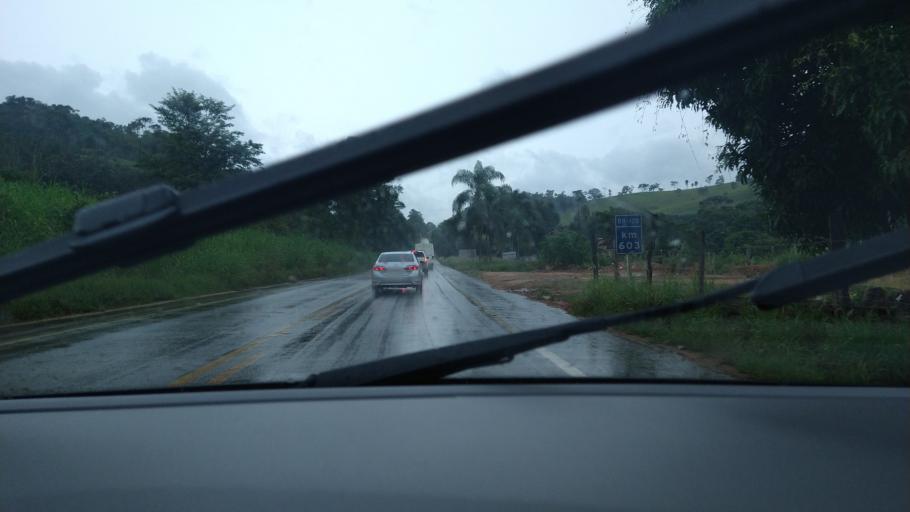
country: BR
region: Minas Gerais
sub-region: Vicosa
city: Vicosa
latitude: -20.6262
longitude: -42.8702
